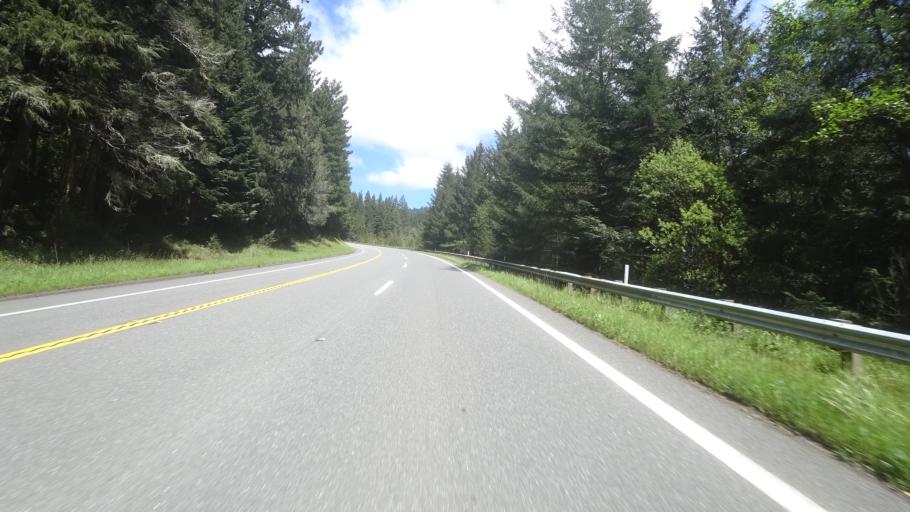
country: US
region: California
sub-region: Humboldt County
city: Blue Lake
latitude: 40.9222
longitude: -123.9095
